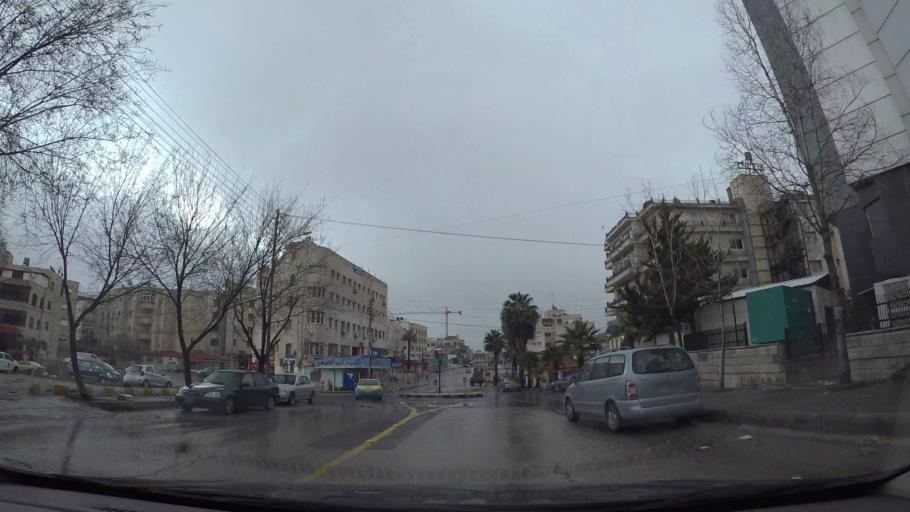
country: JO
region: Amman
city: Wadi as Sir
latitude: 31.9633
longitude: 35.8574
